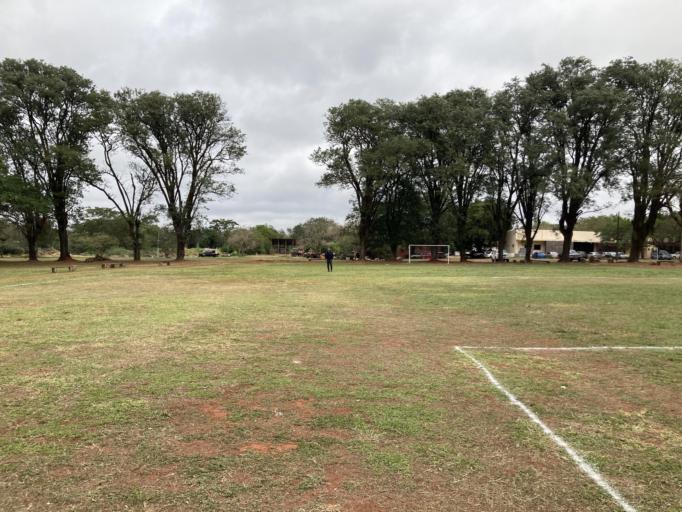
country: PY
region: Central
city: Fernando de la Mora
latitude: -25.3427
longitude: -57.5303
